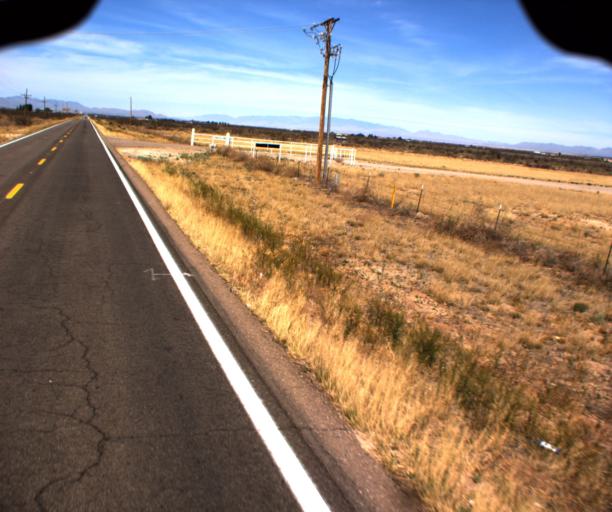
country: US
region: Arizona
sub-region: Cochise County
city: Willcox
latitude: 31.9973
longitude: -109.8595
